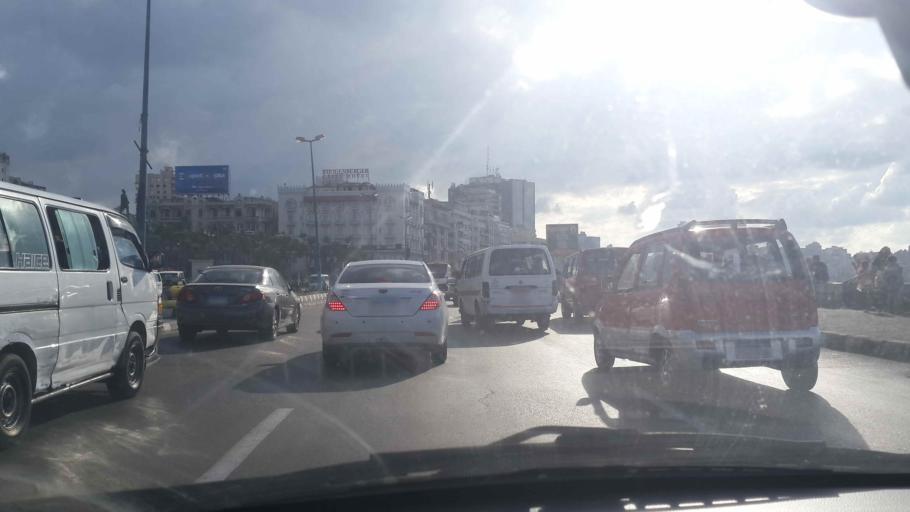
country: EG
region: Alexandria
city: Alexandria
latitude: 31.2021
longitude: 29.9005
